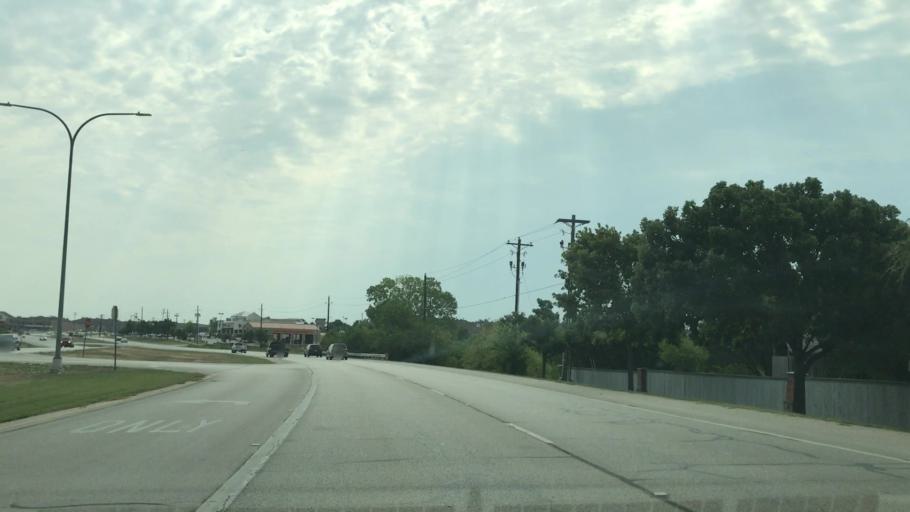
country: US
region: Texas
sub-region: Tarrant County
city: Watauga
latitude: 32.8926
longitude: -97.2784
